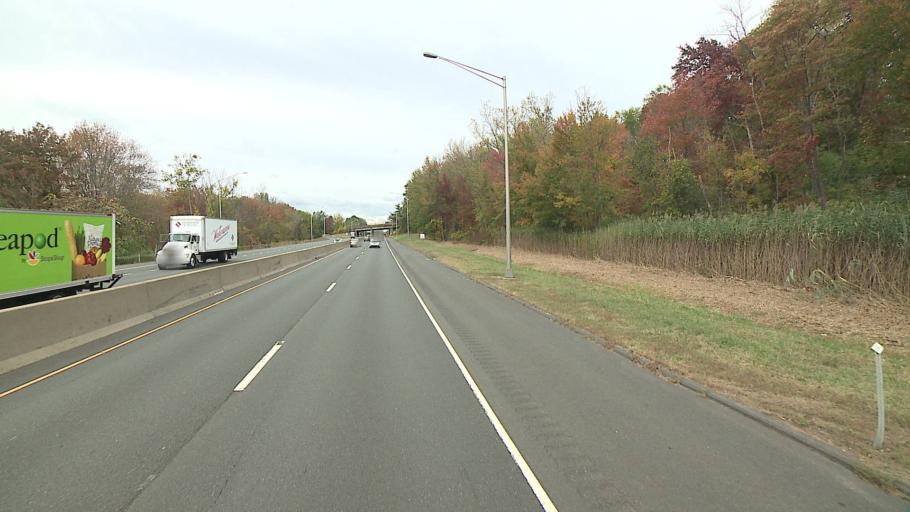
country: US
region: Connecticut
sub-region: Middlesex County
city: Middletown
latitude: 41.5404
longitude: -72.6250
